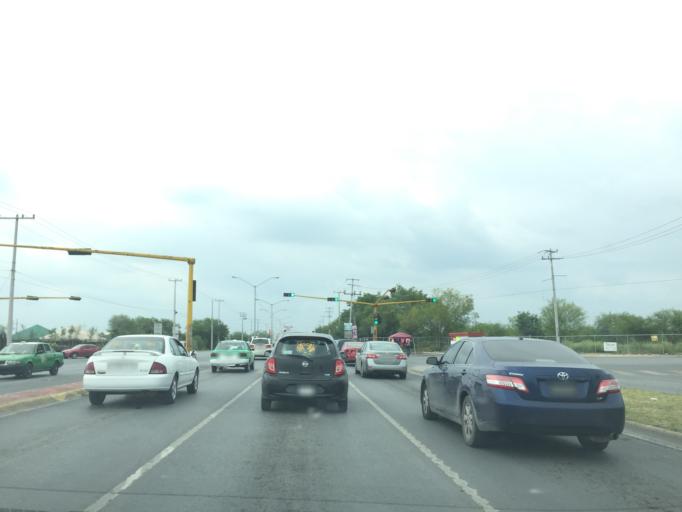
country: MX
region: Nuevo Leon
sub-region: Apodaca
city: Fraccionamiento Cosmopolis Octavo Sector
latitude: 25.7840
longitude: -100.2333
